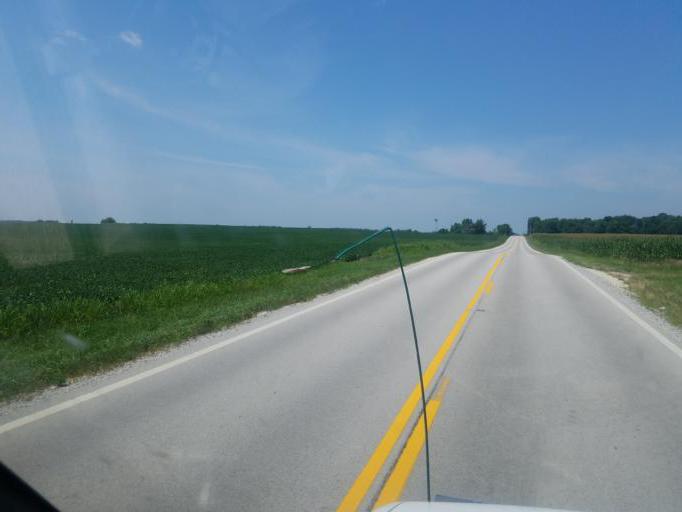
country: US
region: Ohio
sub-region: Auglaize County
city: New Bremen
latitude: 40.4239
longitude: -84.4337
